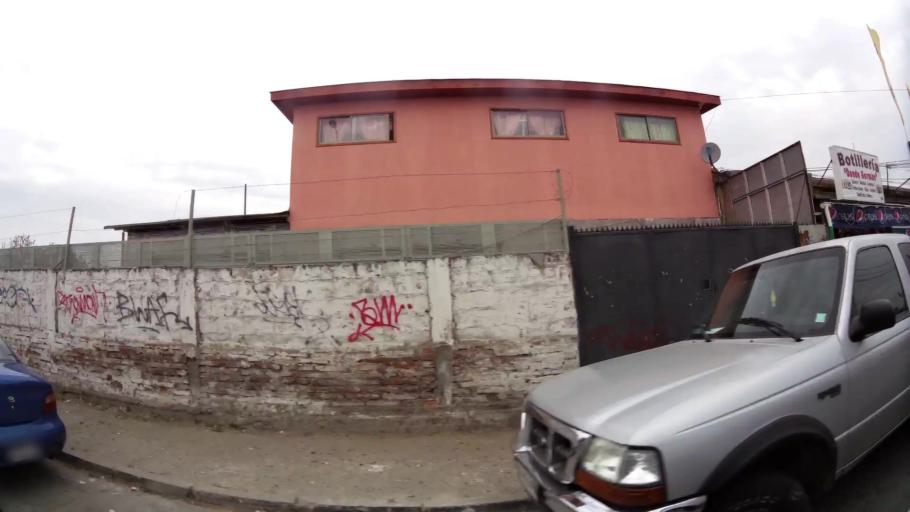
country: CL
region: Santiago Metropolitan
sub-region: Provincia de Santiago
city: Lo Prado
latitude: -33.5001
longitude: -70.7499
